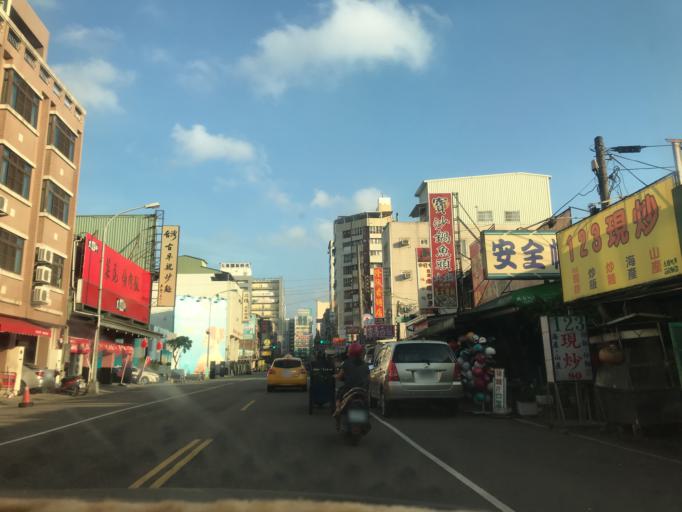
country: TW
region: Taiwan
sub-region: Taichung City
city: Taichung
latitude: 24.1329
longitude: 120.6897
